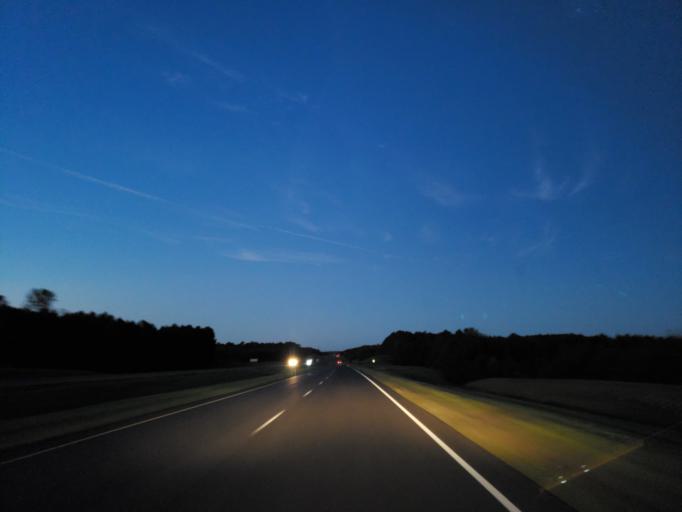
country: US
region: Mississippi
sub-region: Clarke County
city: Quitman
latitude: 32.0098
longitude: -88.6888
